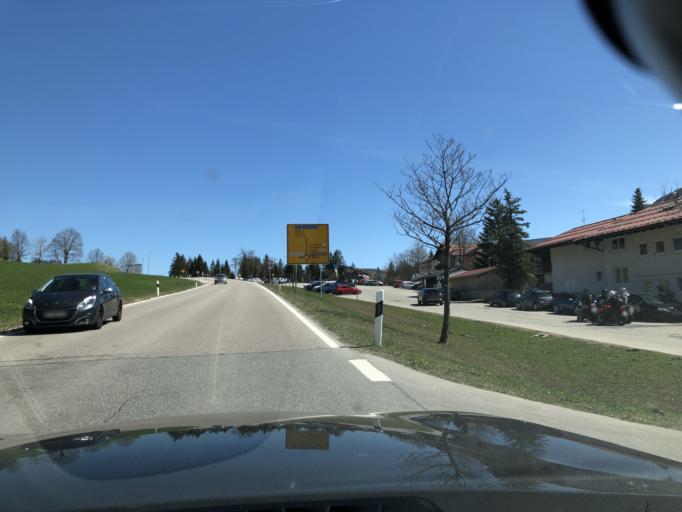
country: AT
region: Tyrol
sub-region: Politischer Bezirk Reutte
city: Schattwald
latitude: 47.5160
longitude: 10.4058
